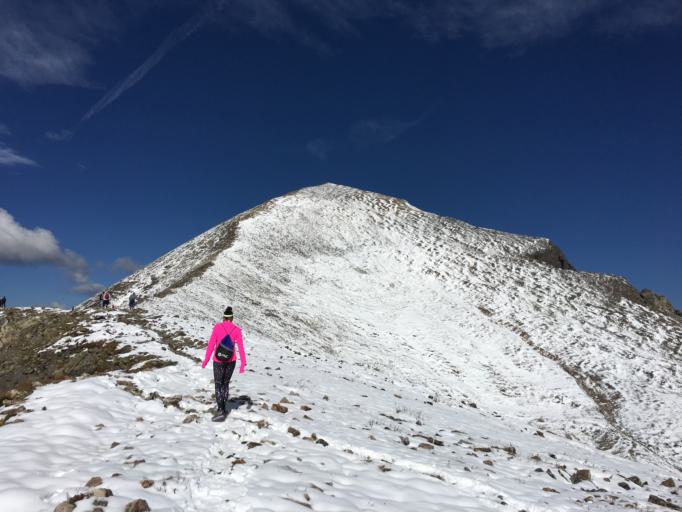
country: US
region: Colorado
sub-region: Summit County
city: Breckenridge
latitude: 39.3950
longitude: -106.0916
